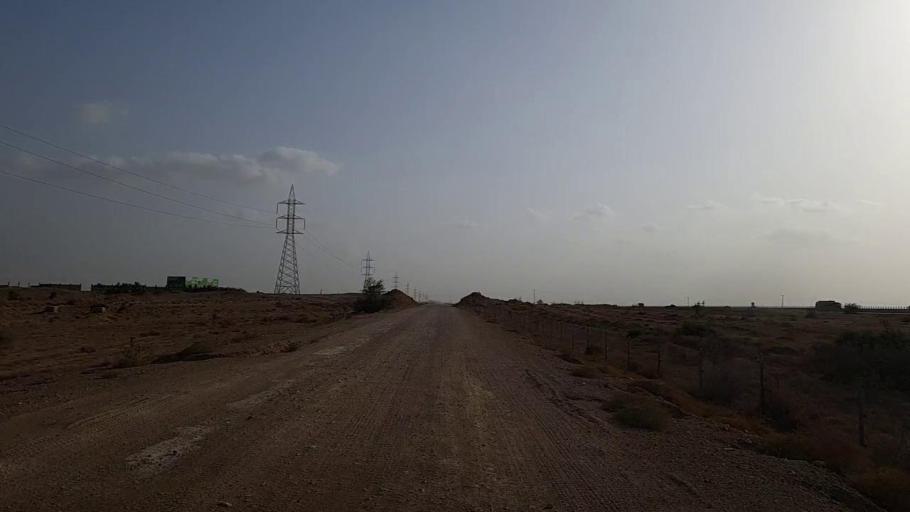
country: PK
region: Sindh
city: Kotri
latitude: 25.2082
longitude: 67.8938
